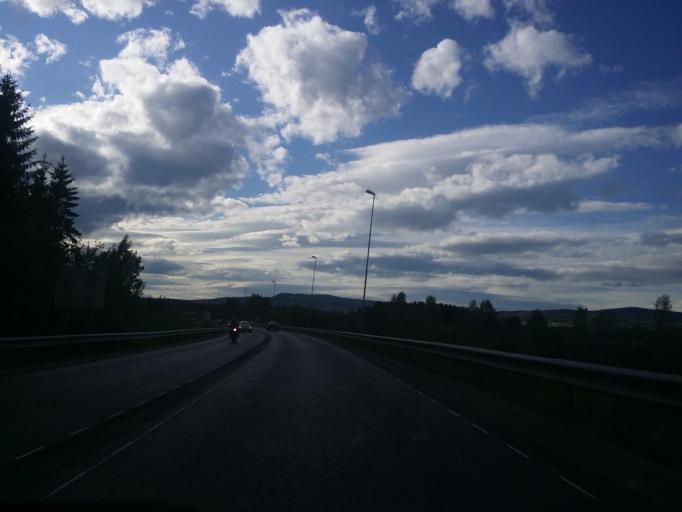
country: NO
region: Hedmark
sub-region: Hamar
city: Hamar
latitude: 60.8301
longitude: 11.0869
